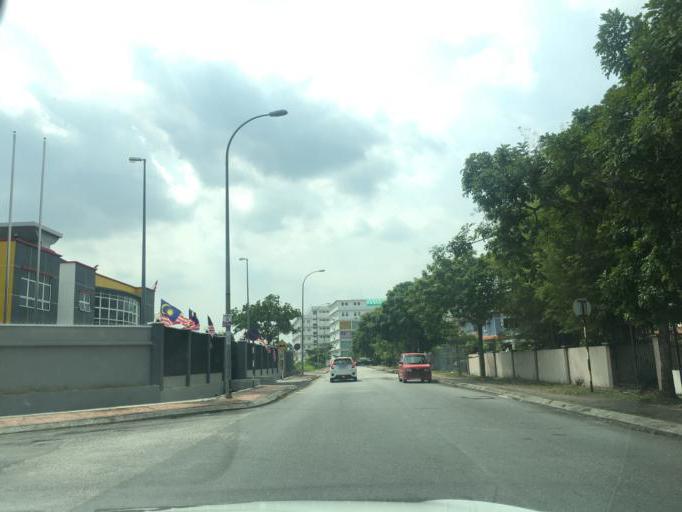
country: MY
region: Selangor
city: Shah Alam
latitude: 3.0769
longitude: 101.4879
